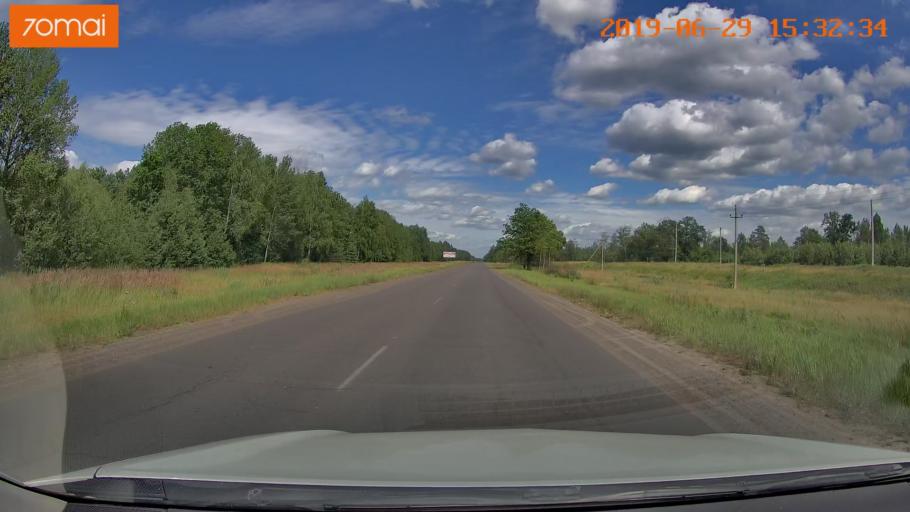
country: BY
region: Brest
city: Mikashevichy
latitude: 52.2102
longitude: 27.4206
